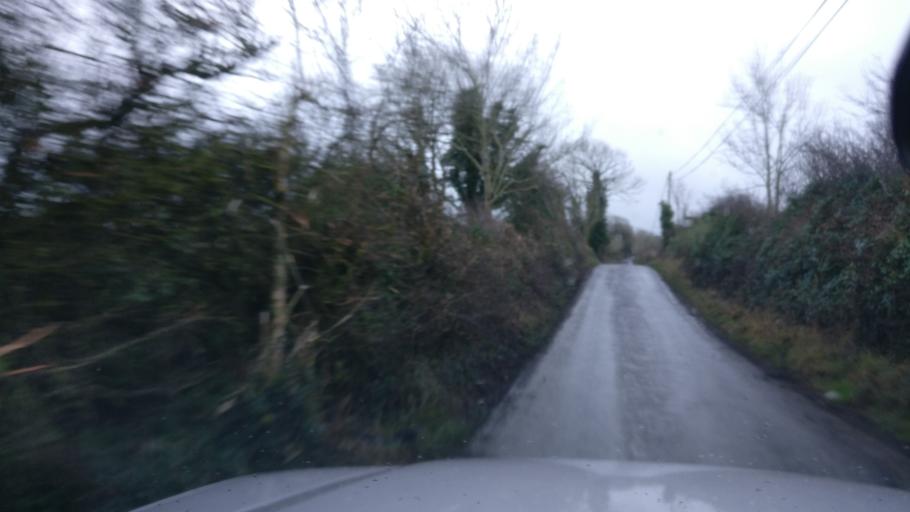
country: IE
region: Connaught
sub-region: County Galway
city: Loughrea
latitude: 53.1929
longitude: -8.6625
